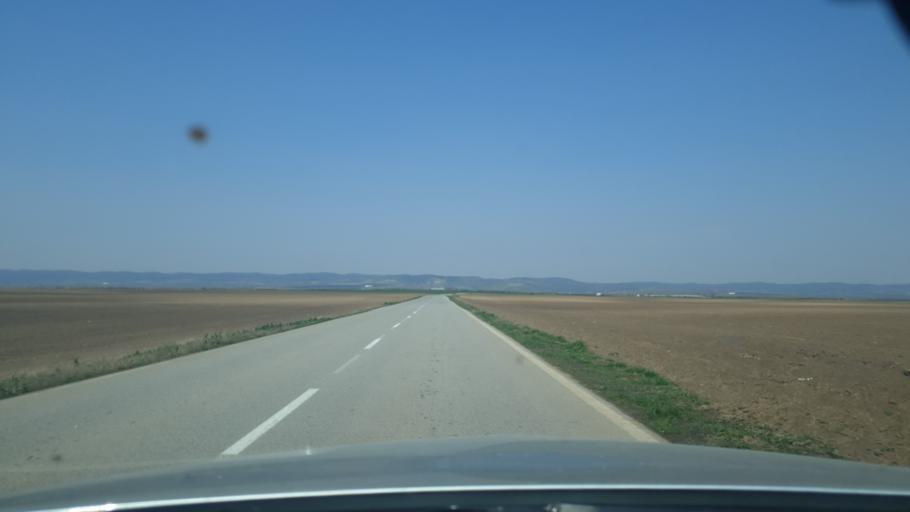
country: RS
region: Autonomna Pokrajina Vojvodina
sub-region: Sremski Okrug
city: Ruma
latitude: 45.0391
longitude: 19.7614
